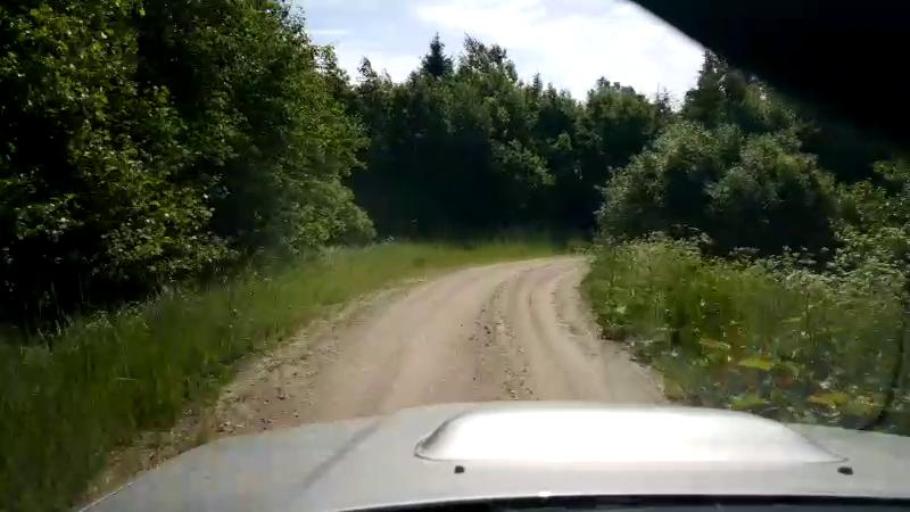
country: EE
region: Paernumaa
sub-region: Sindi linn
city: Sindi
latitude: 58.5288
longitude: 24.6703
